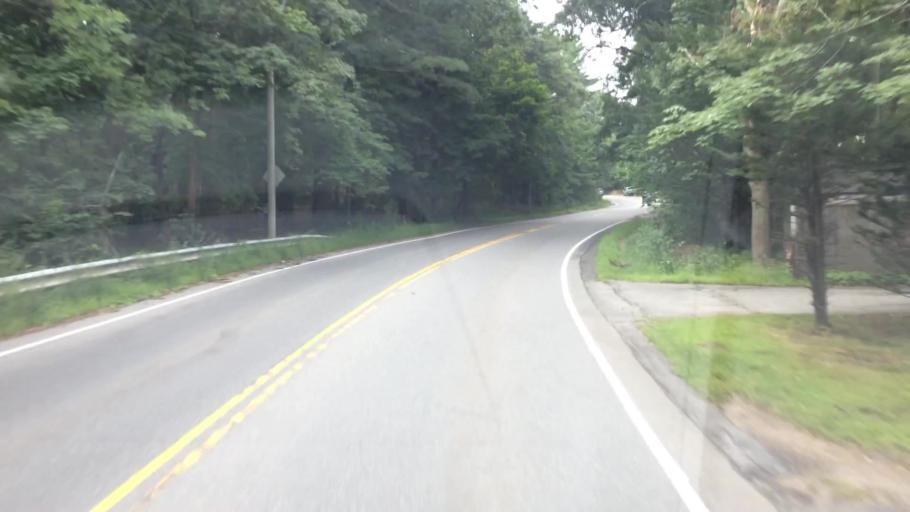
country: US
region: Massachusetts
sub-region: Middlesex County
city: Winchester
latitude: 42.4444
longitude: -71.1243
